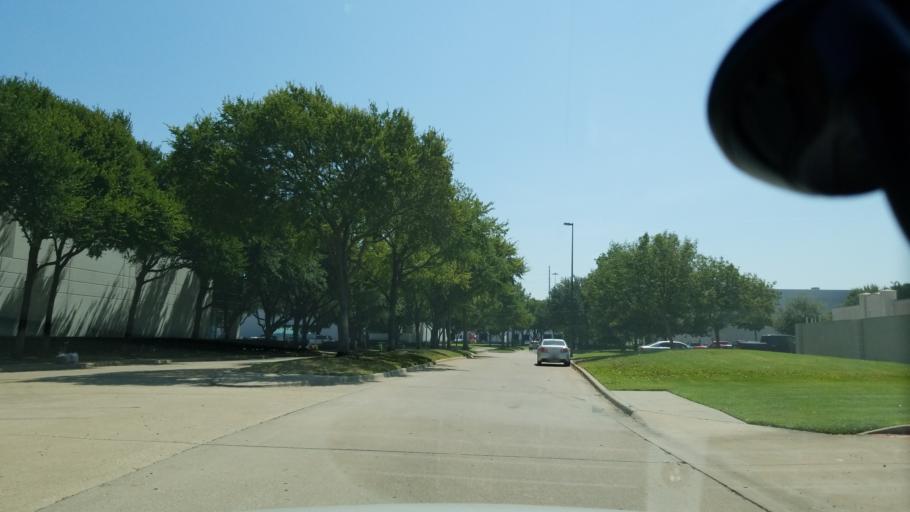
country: US
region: Texas
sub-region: Dallas County
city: Farmers Branch
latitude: 32.9040
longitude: -96.9036
